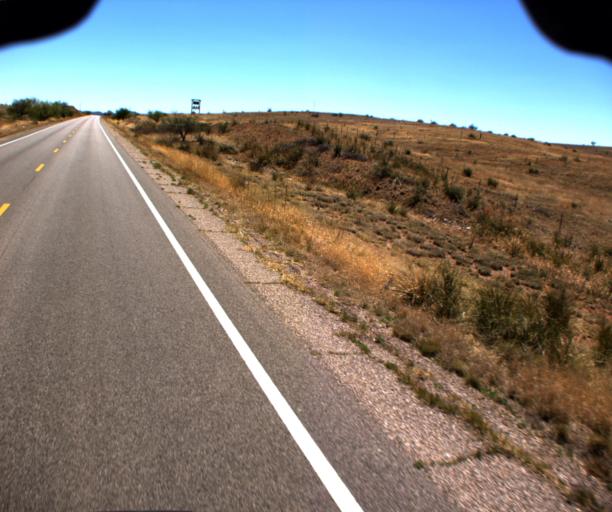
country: US
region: Arizona
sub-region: Pima County
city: Corona de Tucson
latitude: 31.7034
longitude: -110.6555
